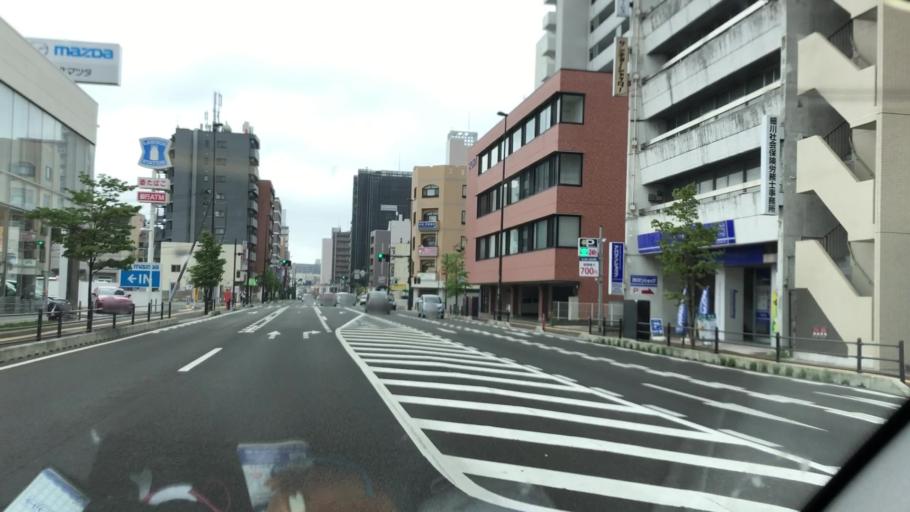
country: JP
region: Miyagi
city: Sendai-shi
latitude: 38.2650
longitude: 140.8873
